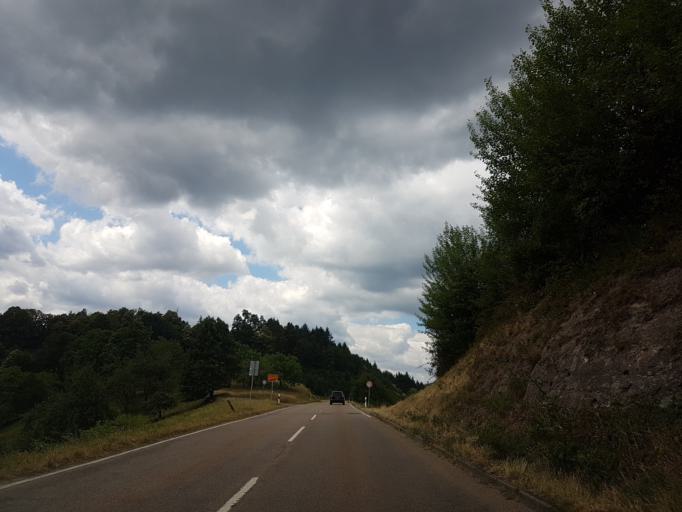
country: DE
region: Baden-Wuerttemberg
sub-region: Karlsruhe Region
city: Loffenau
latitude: 48.7719
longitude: 8.3779
